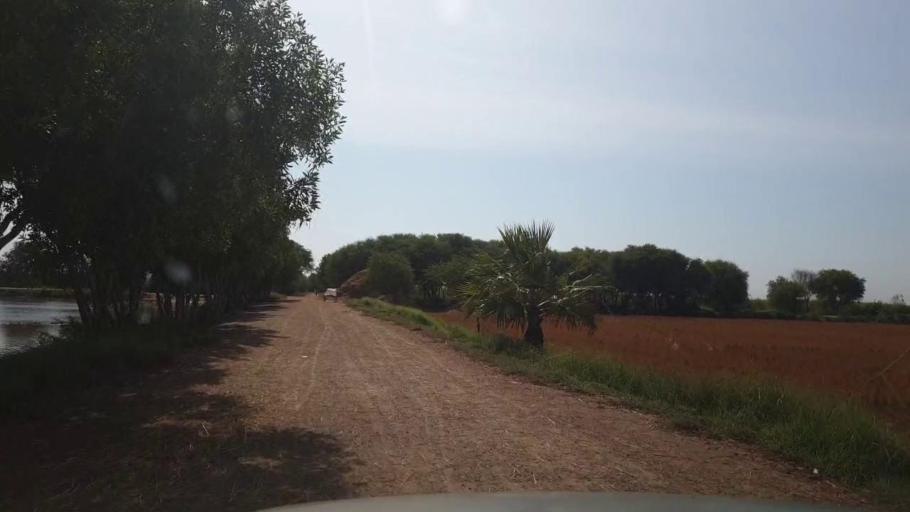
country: PK
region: Sindh
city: Tando Muhammad Khan
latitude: 25.1310
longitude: 68.4200
